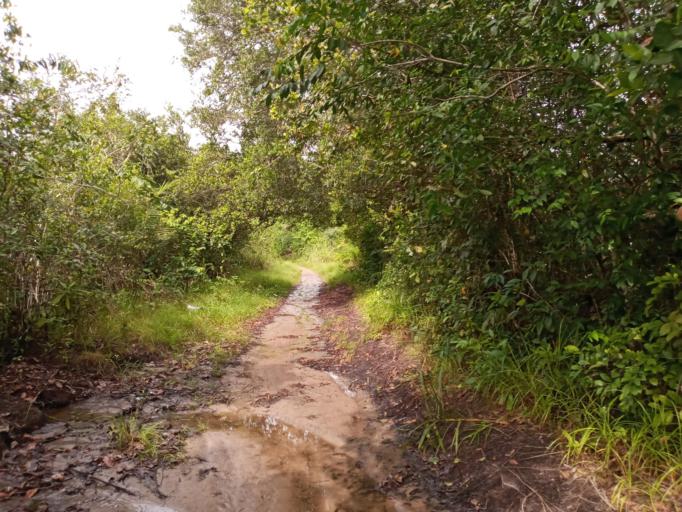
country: SL
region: Southern Province
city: Bonthe
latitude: 7.5128
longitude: -12.5482
